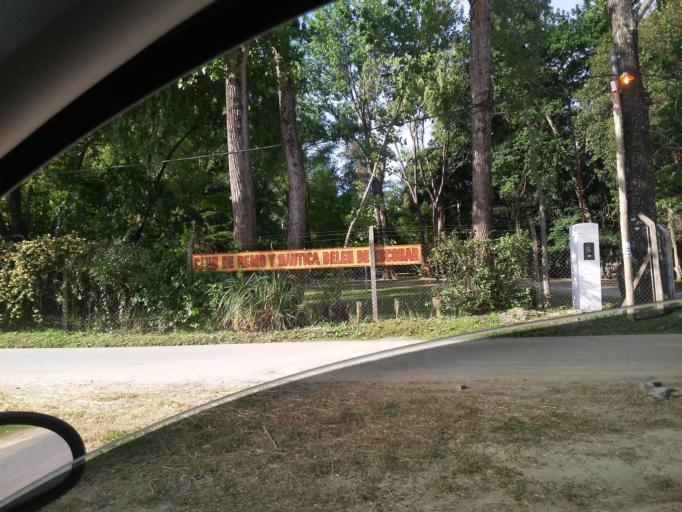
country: AR
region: Buenos Aires
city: Belen de Escobar
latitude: -34.2495
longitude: -58.7286
